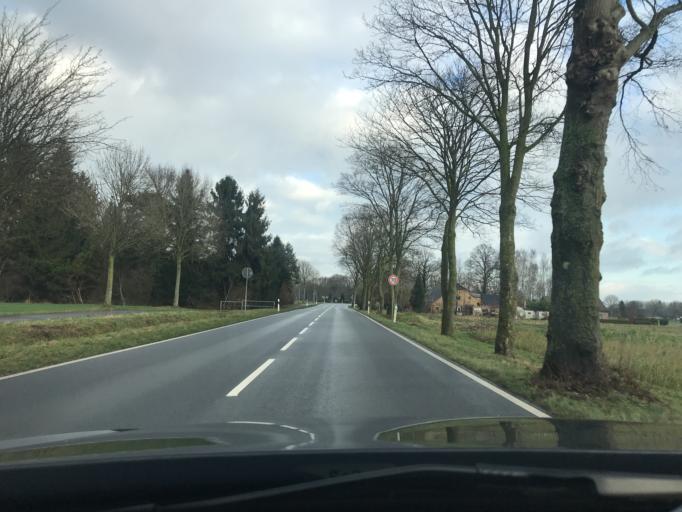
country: DE
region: North Rhine-Westphalia
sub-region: Regierungsbezirk Dusseldorf
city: Grefrath
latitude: 51.3183
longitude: 6.3609
